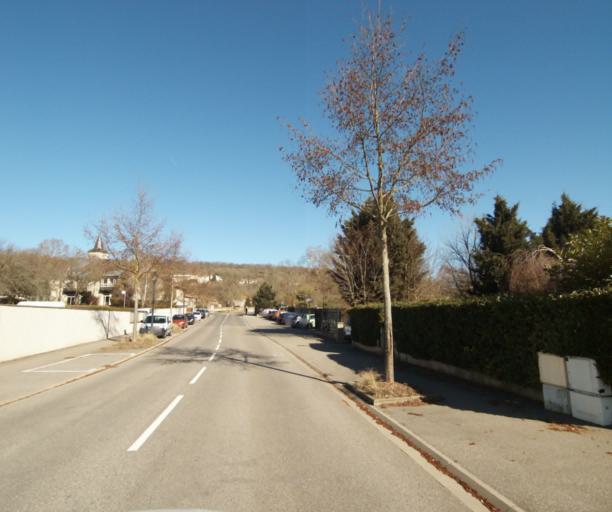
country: FR
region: Lorraine
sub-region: Departement de Meurthe-et-Moselle
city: Ludres
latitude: 48.6196
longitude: 6.1630
